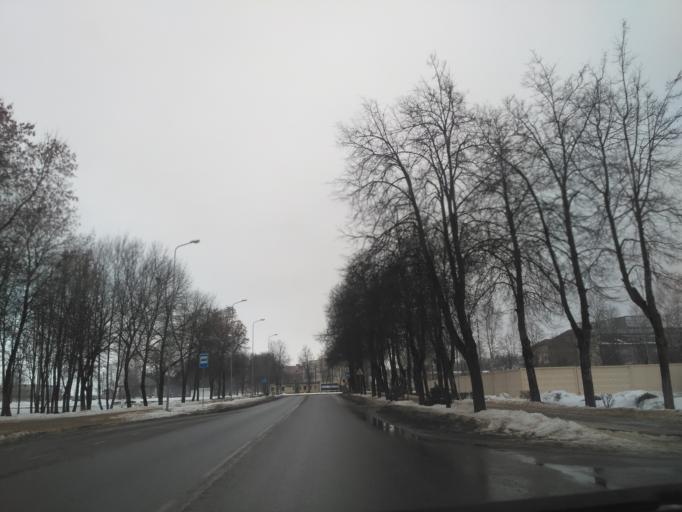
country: BY
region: Minsk
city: Horad Zhodzina
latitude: 54.0942
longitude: 28.3328
